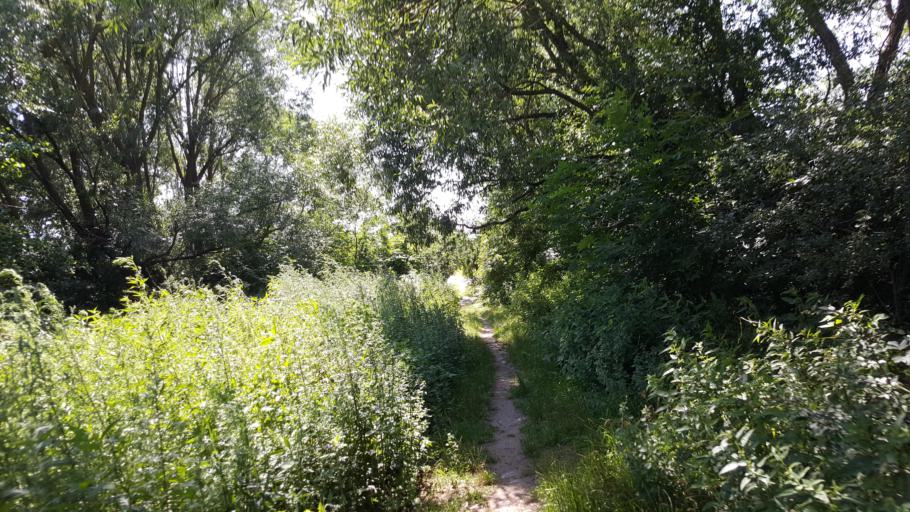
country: BY
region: Brest
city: Vysokaye
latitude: 52.3735
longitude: 23.3732
